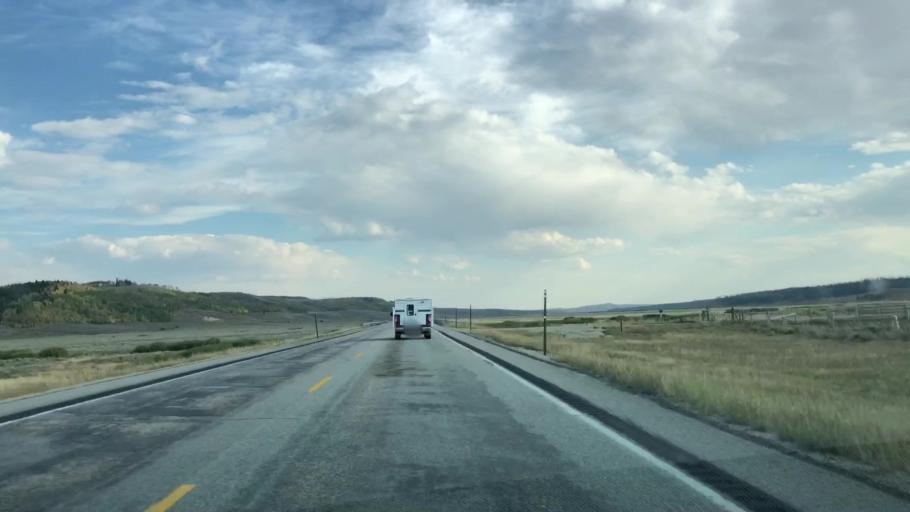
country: US
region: Wyoming
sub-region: Sublette County
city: Pinedale
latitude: 43.1128
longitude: -110.1745
